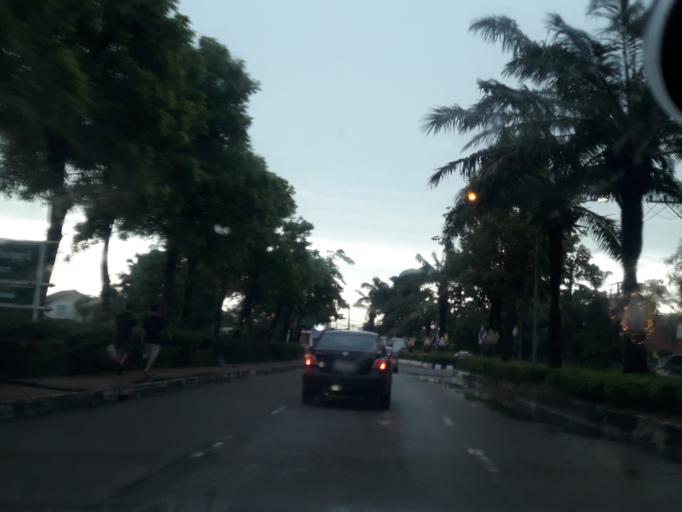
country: TH
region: Pathum Thani
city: Lam Luk Ka
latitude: 13.9372
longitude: 100.7399
